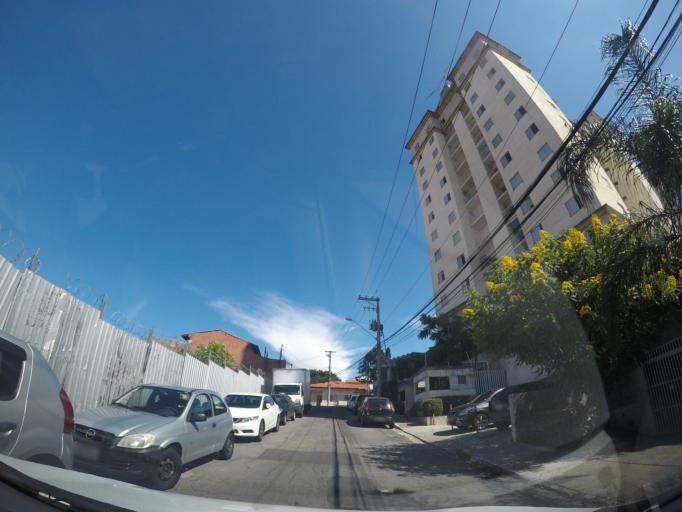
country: BR
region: Sao Paulo
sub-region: Guarulhos
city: Guarulhos
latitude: -23.4522
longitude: -46.5479
